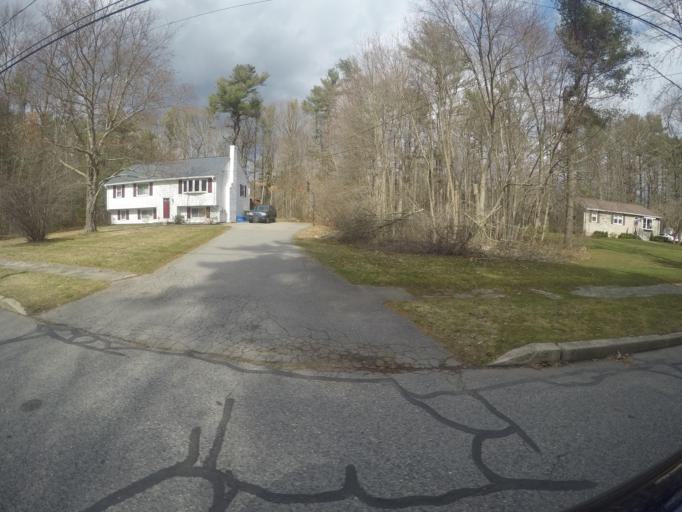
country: US
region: Massachusetts
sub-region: Bristol County
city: Easton
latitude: 42.0372
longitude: -71.1146
